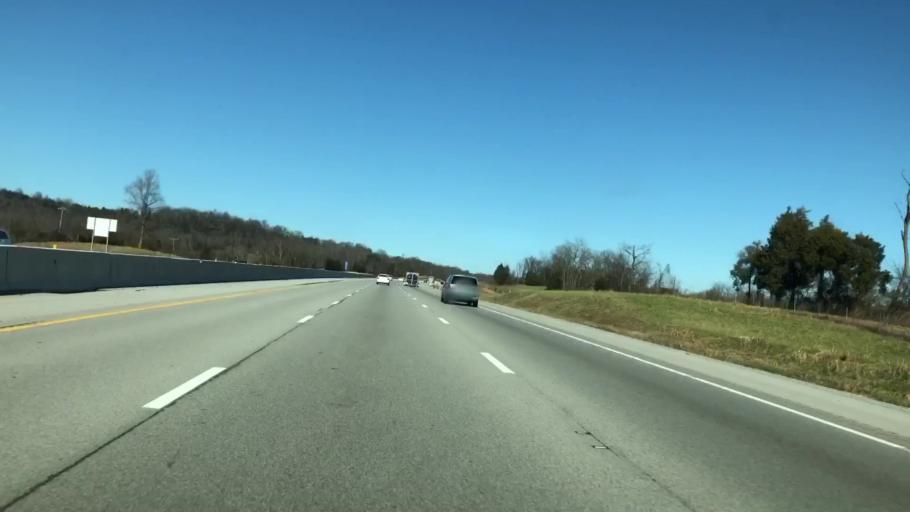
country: US
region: Kentucky
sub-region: Hart County
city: Munfordville
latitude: 37.2584
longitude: -85.9226
